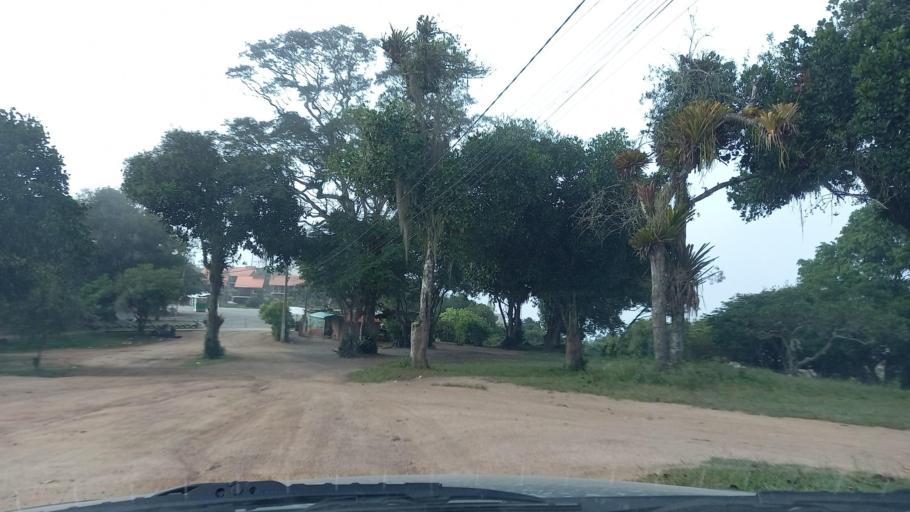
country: BR
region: Pernambuco
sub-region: Bezerros
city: Bezerros
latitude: -8.1636
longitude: -35.7698
